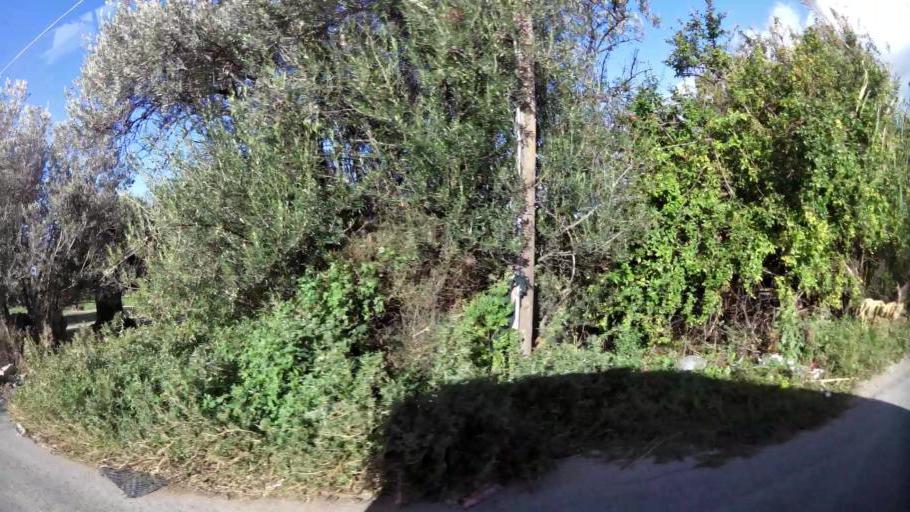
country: GR
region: Attica
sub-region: Nomarchia Athinas
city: Metamorfosi
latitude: 38.0696
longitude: 23.7493
